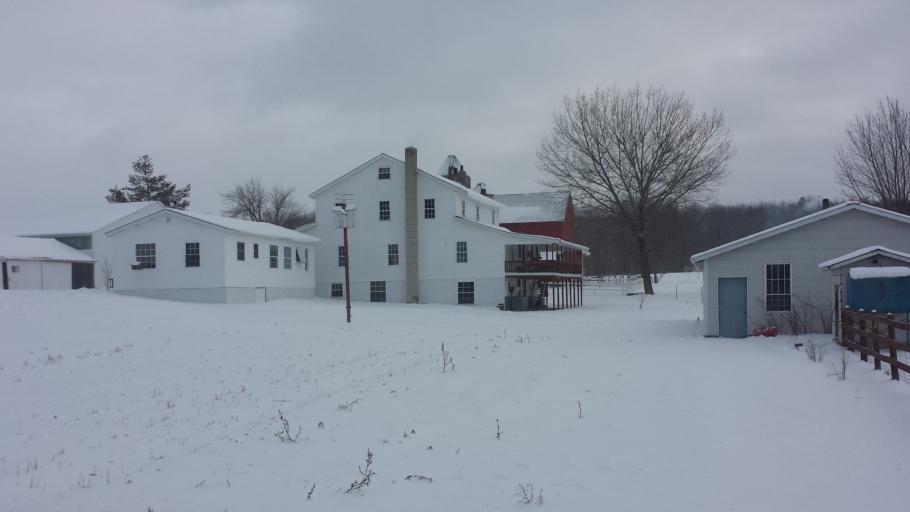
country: US
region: Michigan
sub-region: Montcalm County
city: Lakeview
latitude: 43.4985
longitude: -85.2840
